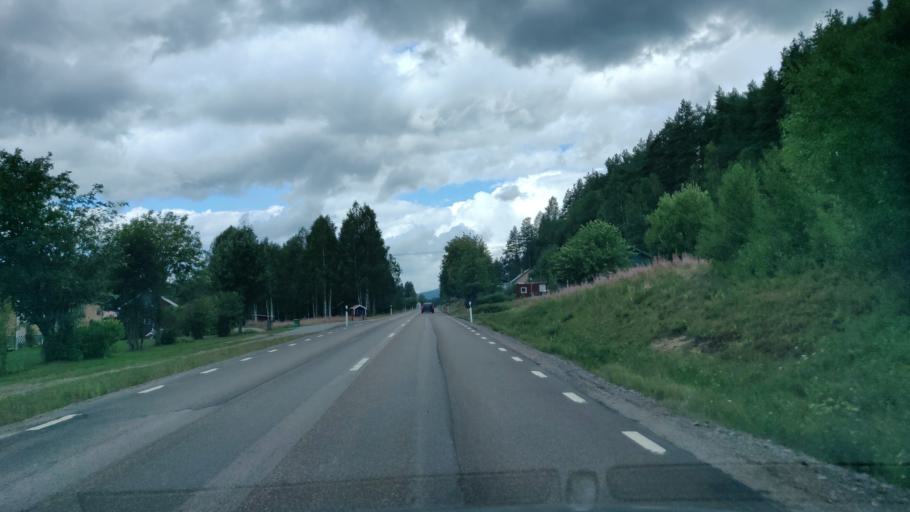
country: SE
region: Vaermland
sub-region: Torsby Kommun
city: Torsby
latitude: 60.5862
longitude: 13.0792
